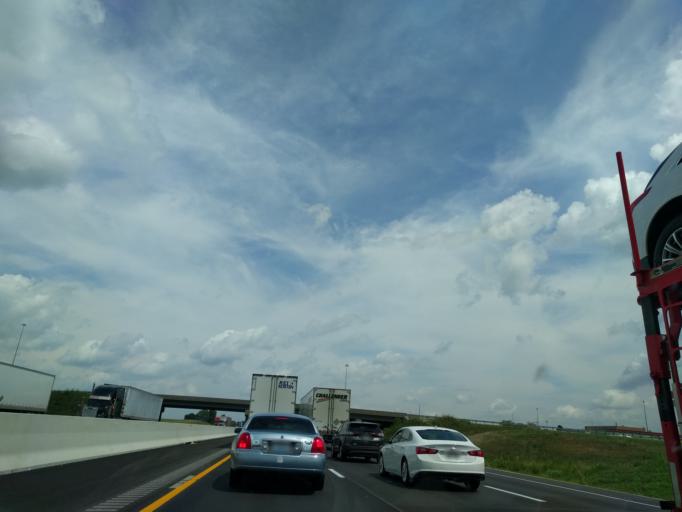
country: US
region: Kentucky
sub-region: Larue County
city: Hodgenville
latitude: 37.5203
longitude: -85.8851
